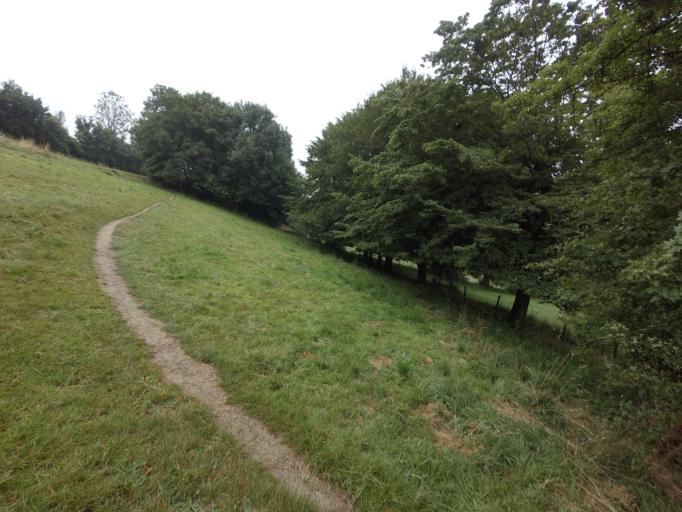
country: BE
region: Wallonia
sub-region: Province de Liege
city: Plombieres
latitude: 50.7562
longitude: 5.9134
